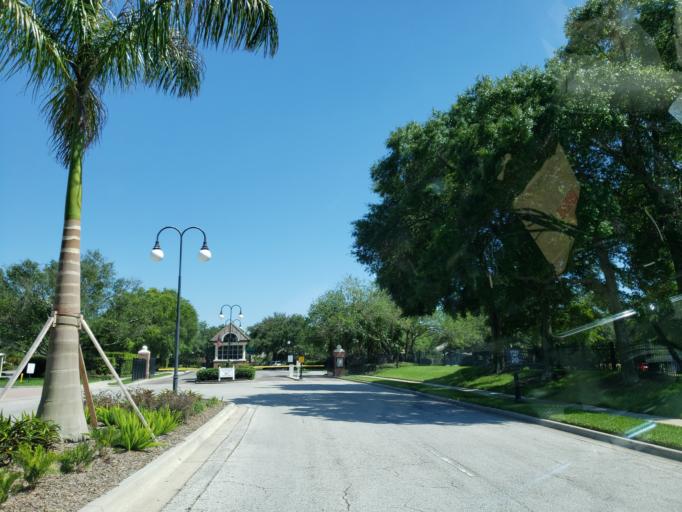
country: US
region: Florida
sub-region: Hillsborough County
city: Tampa
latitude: 27.9367
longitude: -82.4532
